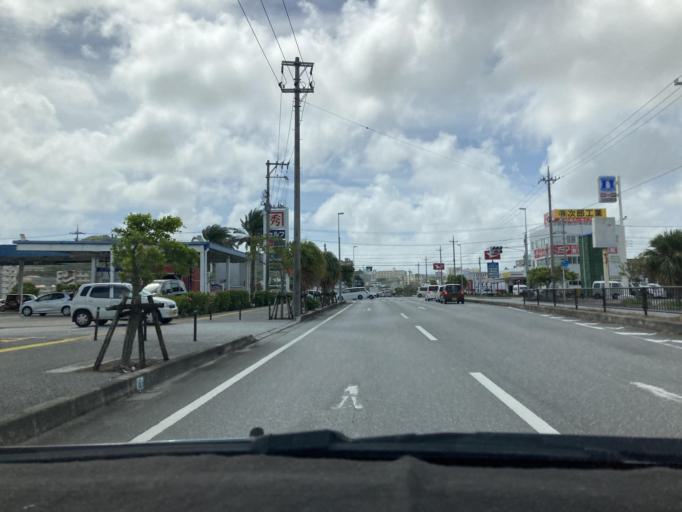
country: JP
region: Okinawa
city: Ginowan
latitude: 26.2064
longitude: 127.7626
